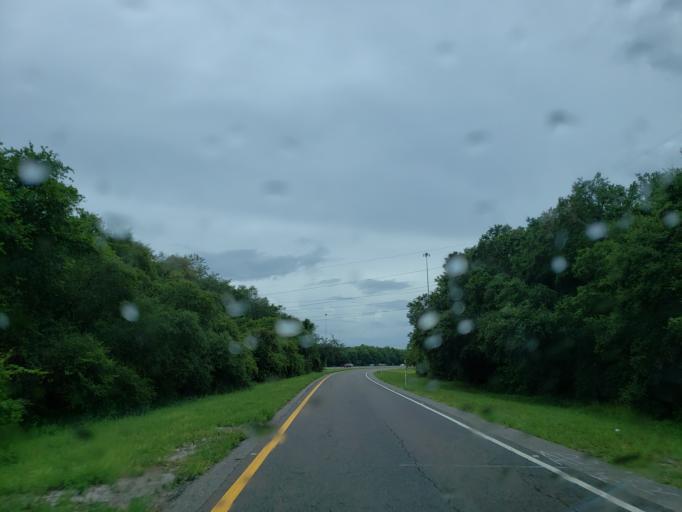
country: US
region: Florida
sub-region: Hillsborough County
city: Apollo Beach
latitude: 27.7888
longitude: -82.3592
